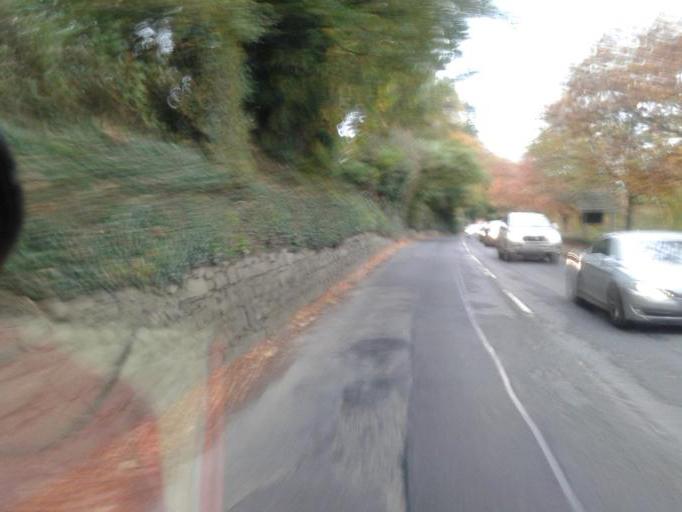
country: IE
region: Munster
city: Ballina
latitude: 52.8056
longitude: -8.4348
